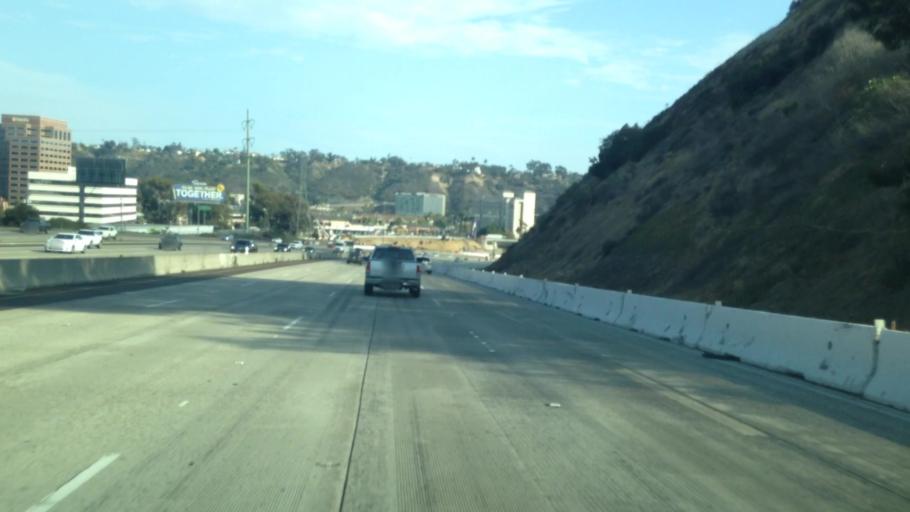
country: US
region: California
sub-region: San Diego County
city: San Diego
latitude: 32.7762
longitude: -117.1621
